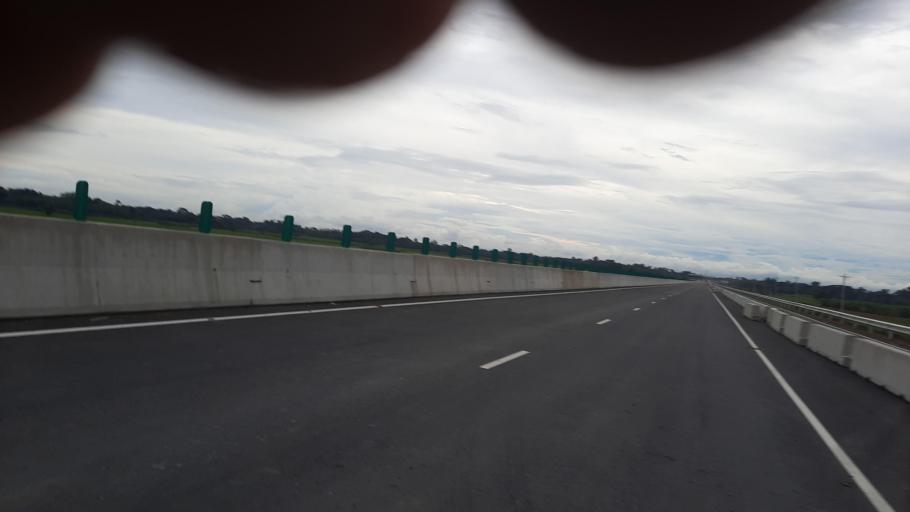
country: BD
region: Khulna
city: Kalia
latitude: 23.2029
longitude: 89.7084
